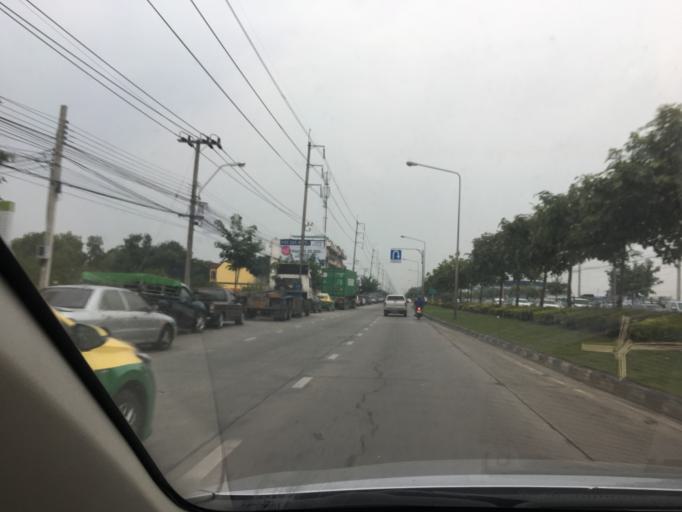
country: TH
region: Bangkok
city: Lat Krabang
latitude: 13.7527
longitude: 100.7751
